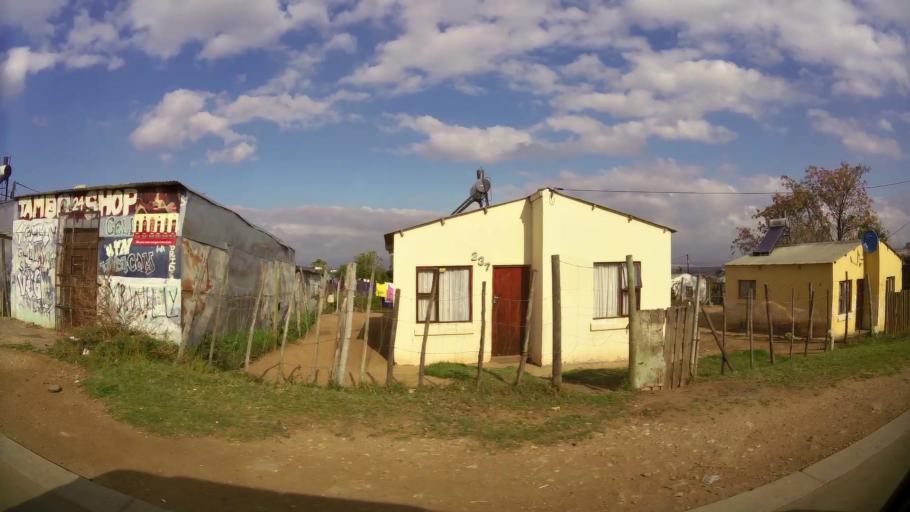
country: ZA
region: Eastern Cape
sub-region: Nelson Mandela Bay Metropolitan Municipality
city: Uitenhage
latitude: -33.7314
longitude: 25.3957
